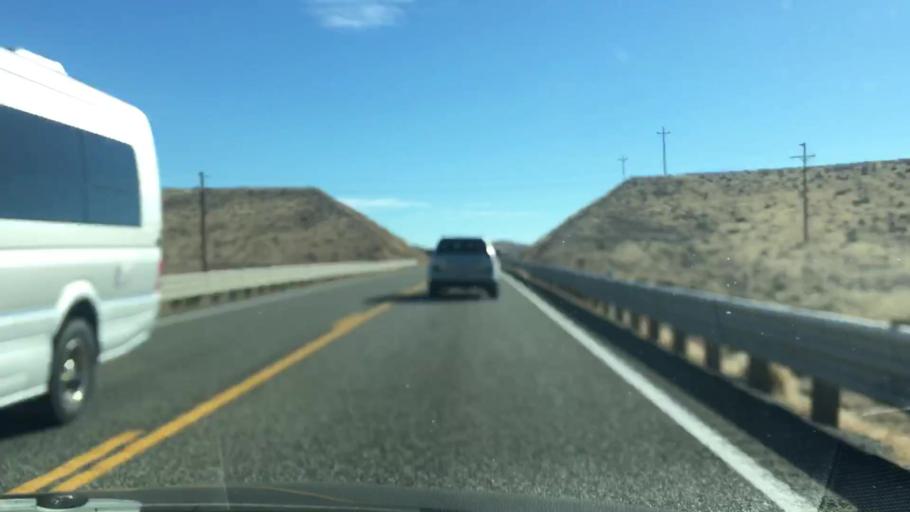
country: US
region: Nevada
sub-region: Lyon County
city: Silver Springs
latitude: 39.2157
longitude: -119.2207
